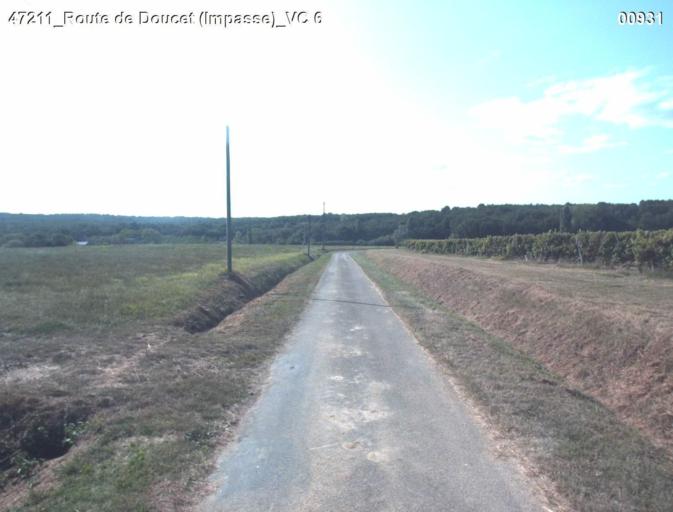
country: FR
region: Midi-Pyrenees
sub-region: Departement du Gers
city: Montreal
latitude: 44.0150
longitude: 0.2033
